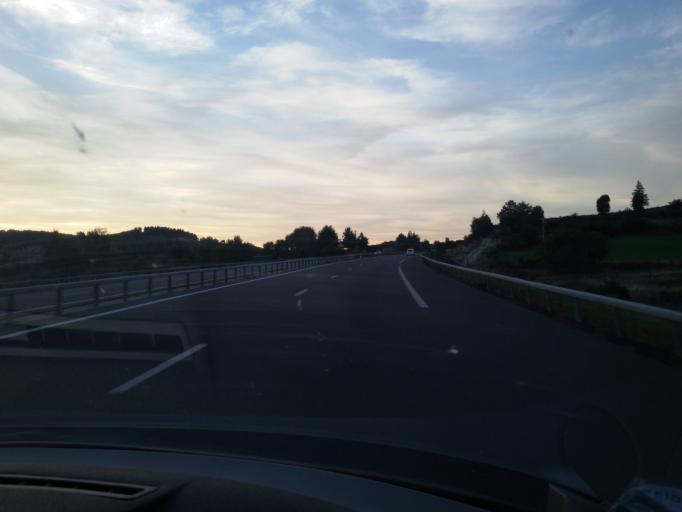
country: FR
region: Languedoc-Roussillon
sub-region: Departement de la Lozere
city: Marvejols
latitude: 44.6247
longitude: 3.2470
